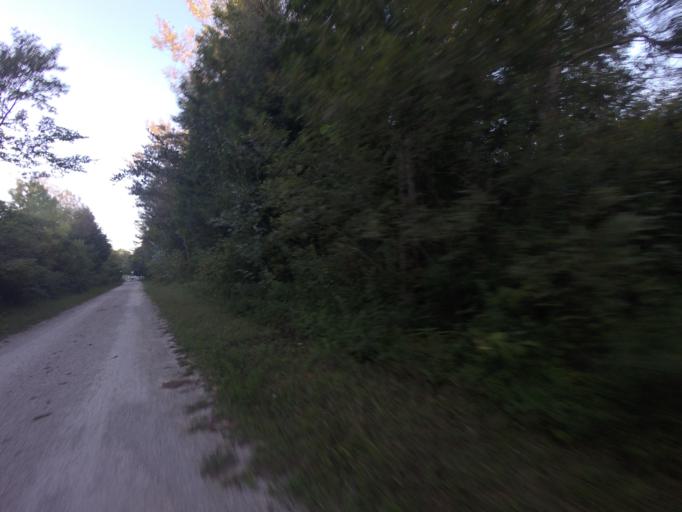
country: CA
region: Ontario
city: Brampton
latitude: 43.9007
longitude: -79.8393
